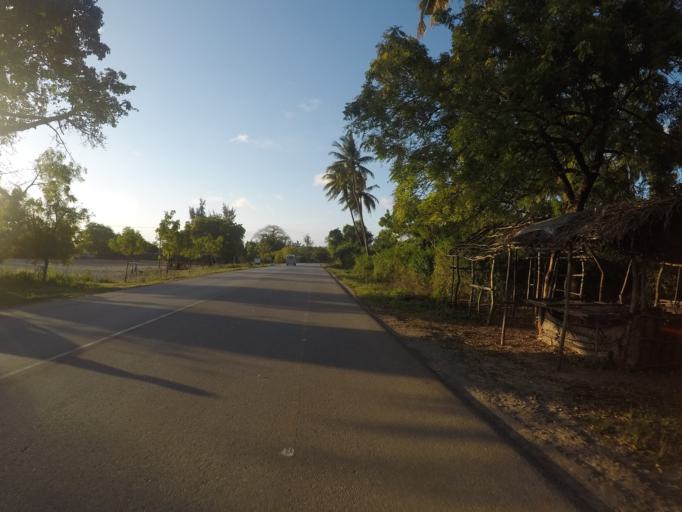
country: TZ
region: Zanzibar North
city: Kijini
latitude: -5.8236
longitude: 39.2916
